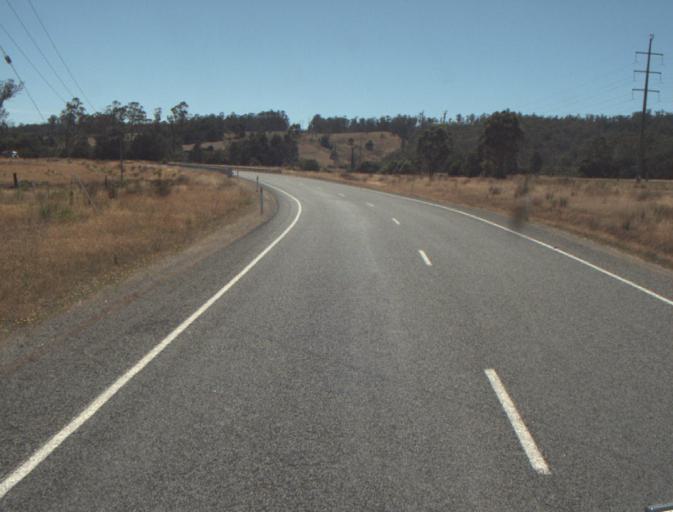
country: AU
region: Tasmania
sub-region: Launceston
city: Newstead
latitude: -41.3618
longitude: 147.3363
